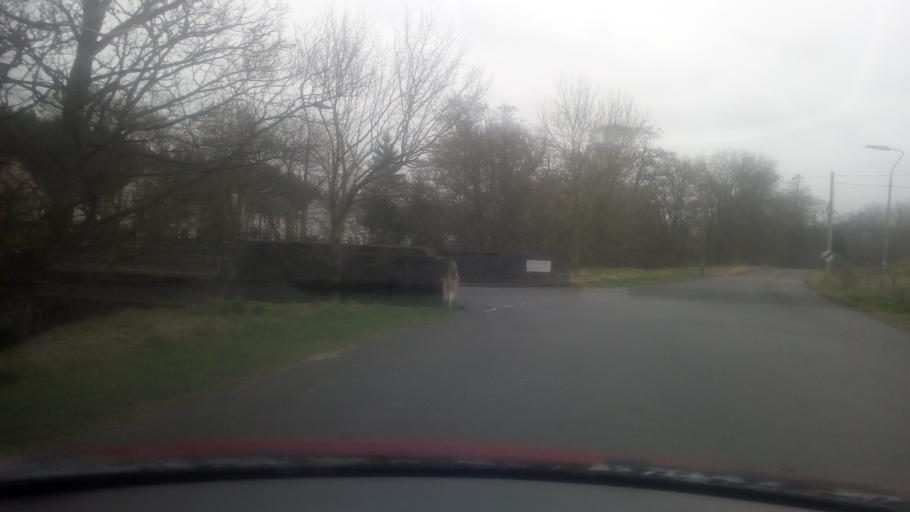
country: GB
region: Scotland
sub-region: The Scottish Borders
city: Jedburgh
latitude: 55.3983
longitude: -2.6551
